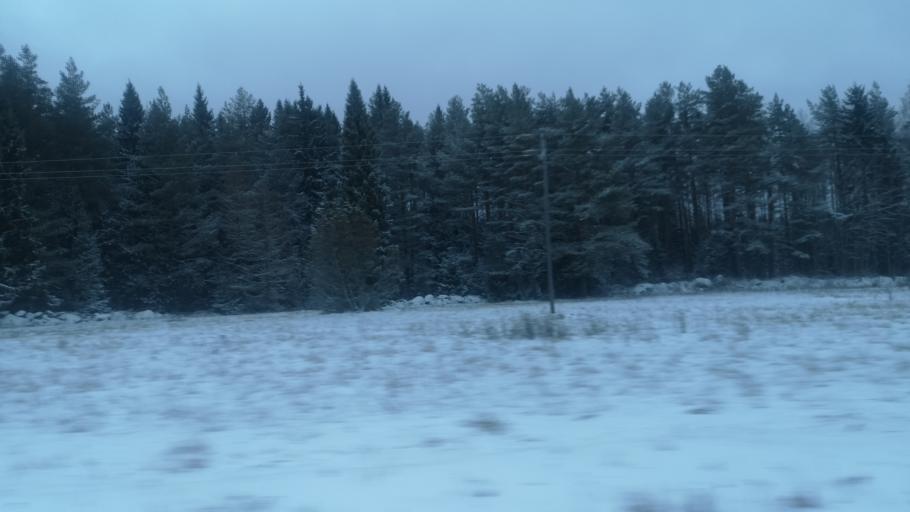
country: FI
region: Southern Savonia
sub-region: Savonlinna
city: Savonlinna
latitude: 62.0053
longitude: 28.7377
